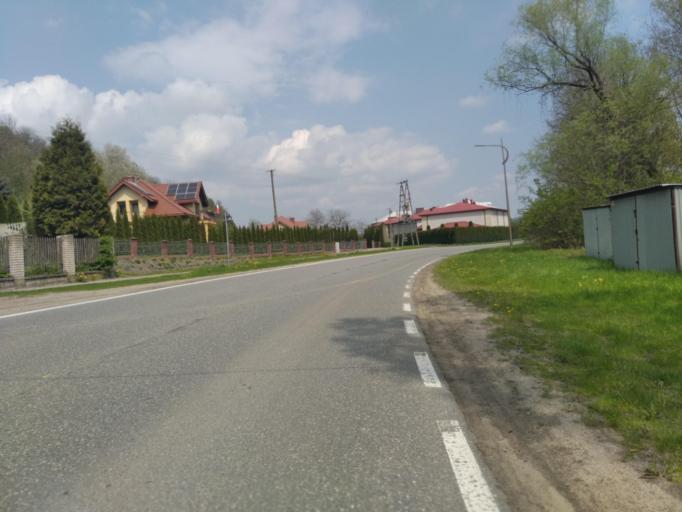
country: PL
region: Subcarpathian Voivodeship
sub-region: Powiat krosnienski
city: Rymanow
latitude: 49.5616
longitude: 21.8576
